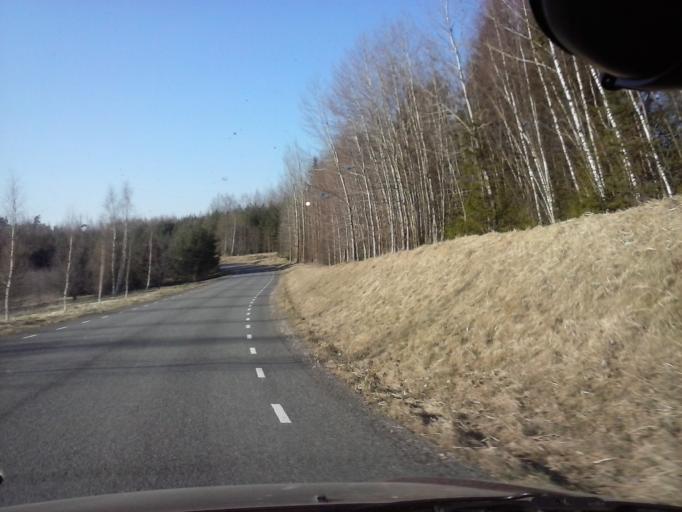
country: EE
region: Tartu
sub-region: UElenurme vald
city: Ulenurme
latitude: 58.1624
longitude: 26.8481
